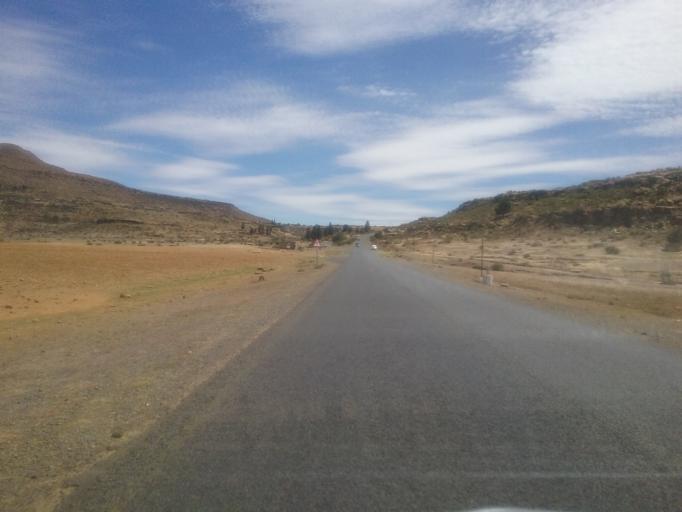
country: LS
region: Mohale's Hoek District
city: Mohale's Hoek
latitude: -30.0861
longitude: 27.4297
